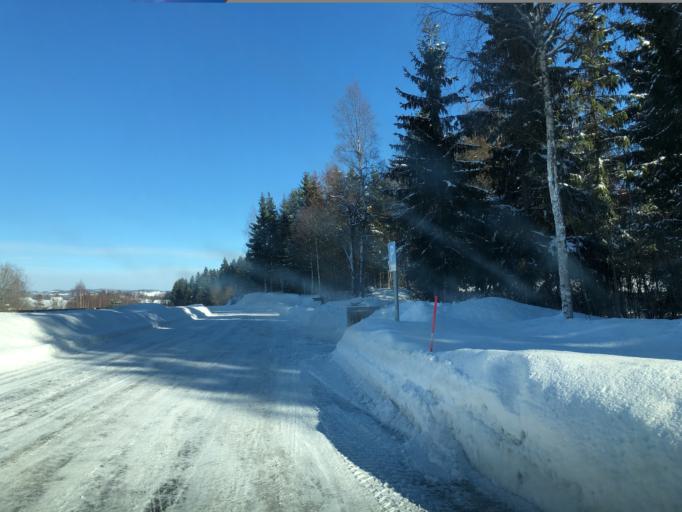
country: NO
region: Oppland
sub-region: Lunner
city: Roa
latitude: 60.2784
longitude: 10.5197
